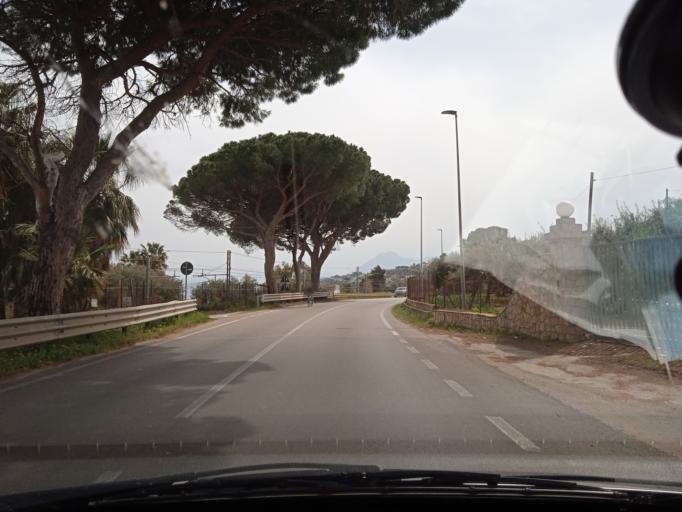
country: IT
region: Sicily
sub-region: Palermo
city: Torre Colonna-Sperone
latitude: 38.0398
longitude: 13.5638
